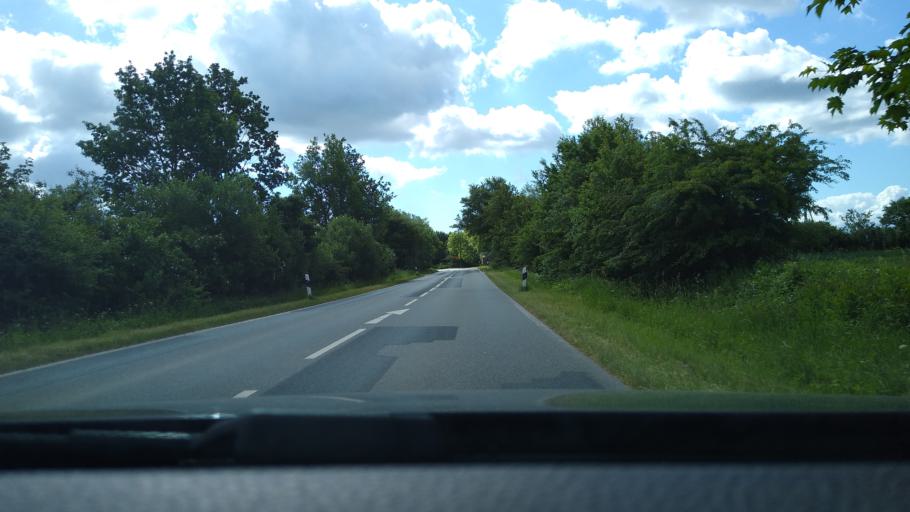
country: DE
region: Schleswig-Holstein
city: Riepsdorf
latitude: 54.2093
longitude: 10.9495
